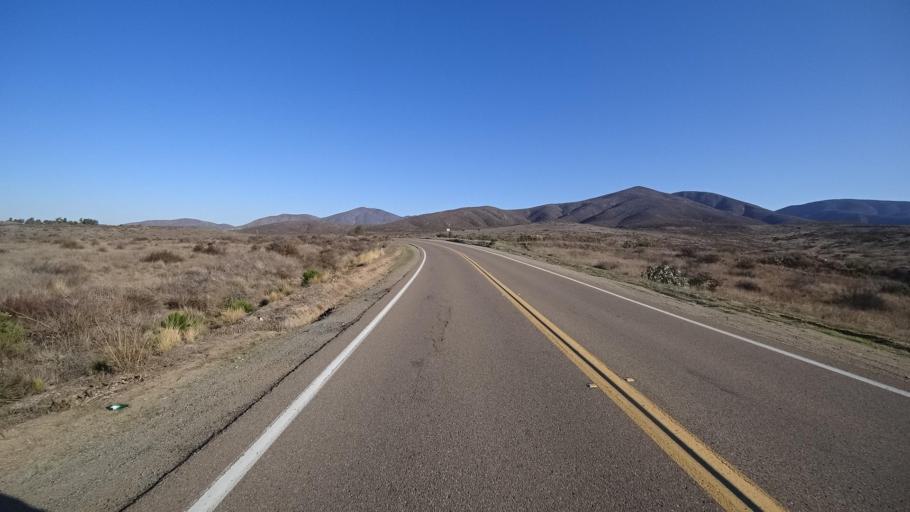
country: US
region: California
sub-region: San Diego County
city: Jamul
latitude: 32.6383
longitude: -116.9224
